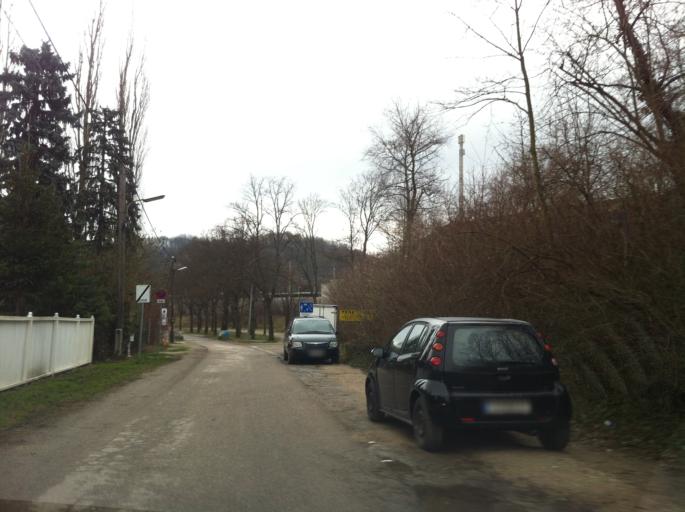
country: AT
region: Lower Austria
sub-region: Politischer Bezirk Wien-Umgebung
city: Purkersdorf
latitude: 48.2071
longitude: 16.1985
